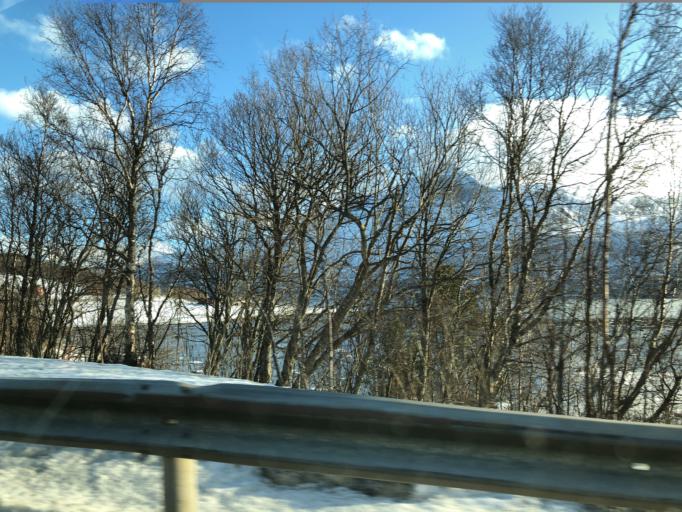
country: NO
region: Nordland
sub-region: Narvik
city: Bjerkvik
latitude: 68.4795
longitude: 17.5556
